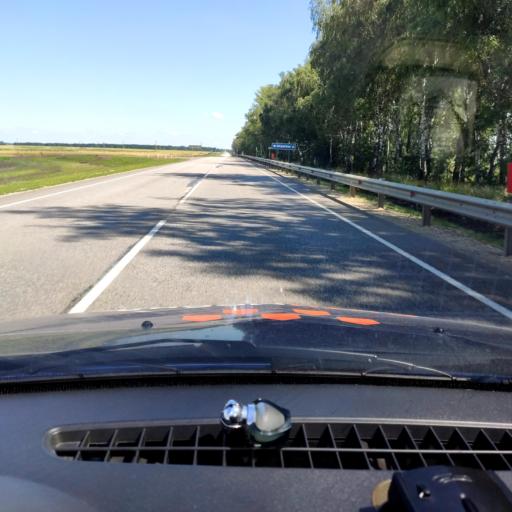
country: RU
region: Orjol
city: Pokrovskoye
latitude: 52.6334
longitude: 36.6943
